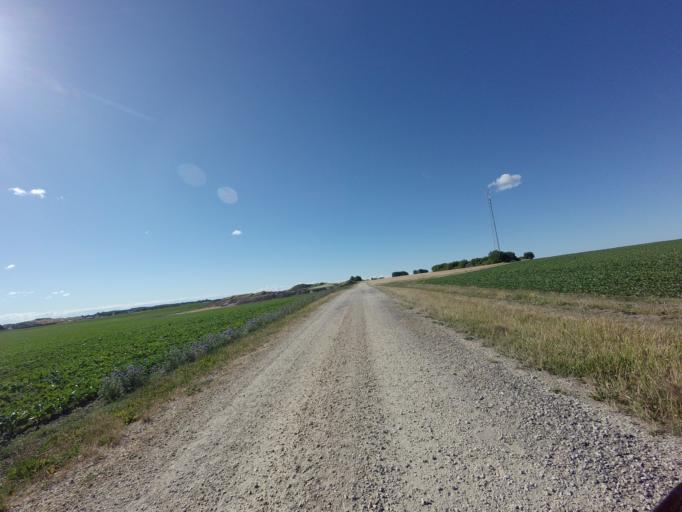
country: SE
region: Skane
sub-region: Trelleborgs Kommun
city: Skare
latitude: 55.3892
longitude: 13.0709
